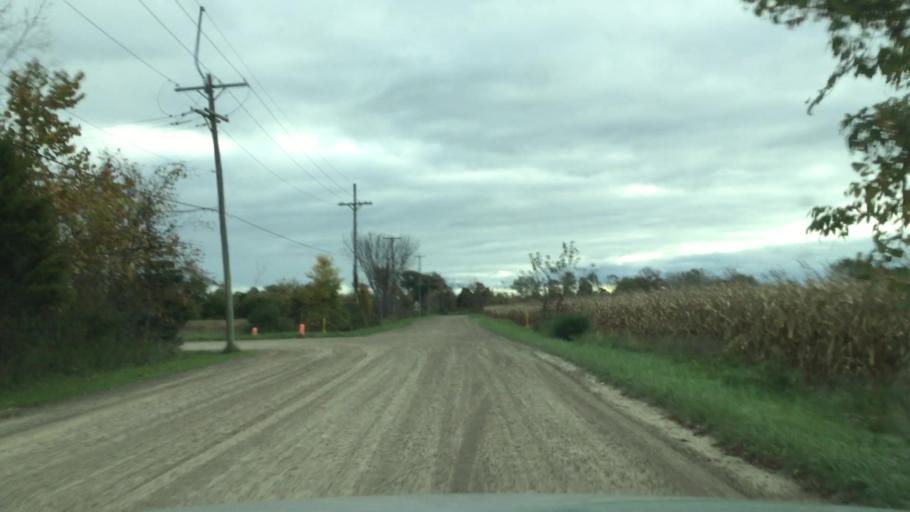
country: US
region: Michigan
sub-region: Macomb County
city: Richmond
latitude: 42.8225
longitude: -82.7453
